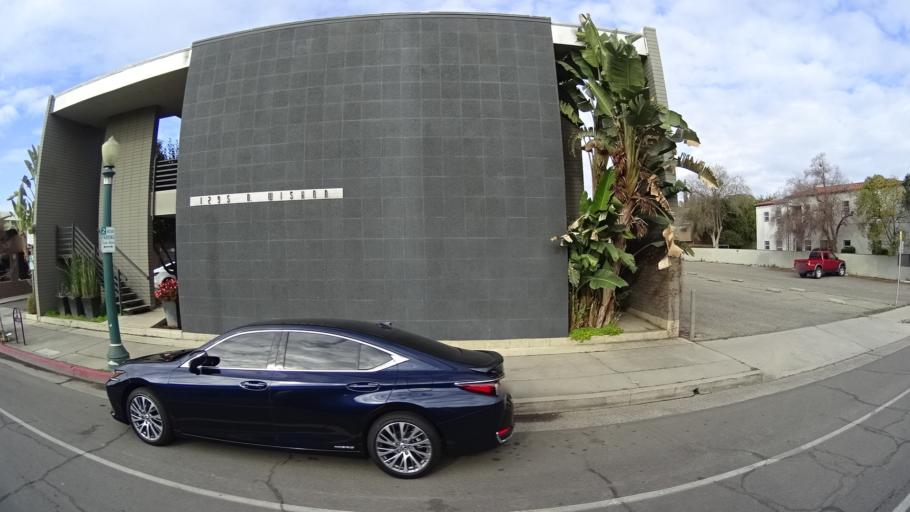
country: US
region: California
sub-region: Fresno County
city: Fresno
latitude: 36.7594
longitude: -119.8011
